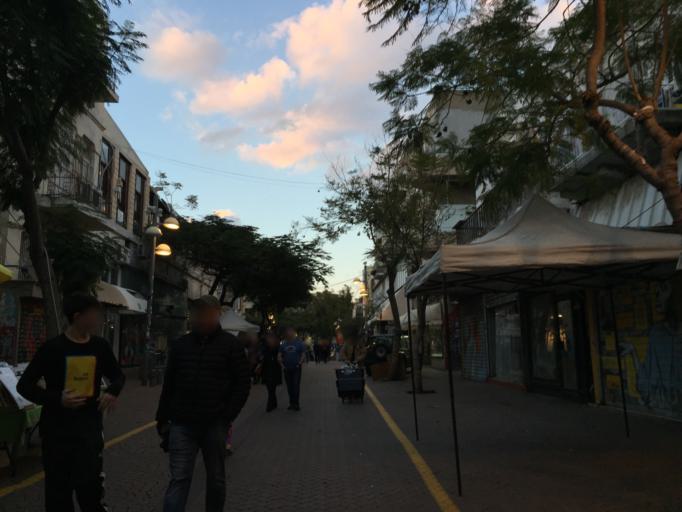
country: IL
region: Tel Aviv
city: Tel Aviv
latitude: 32.0670
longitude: 34.7703
